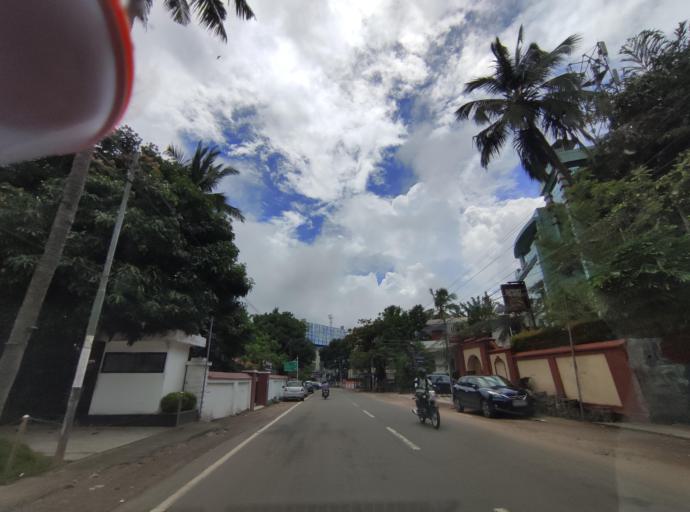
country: IN
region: Kerala
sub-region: Thiruvananthapuram
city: Thiruvananthapuram
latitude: 8.4998
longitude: 76.9598
